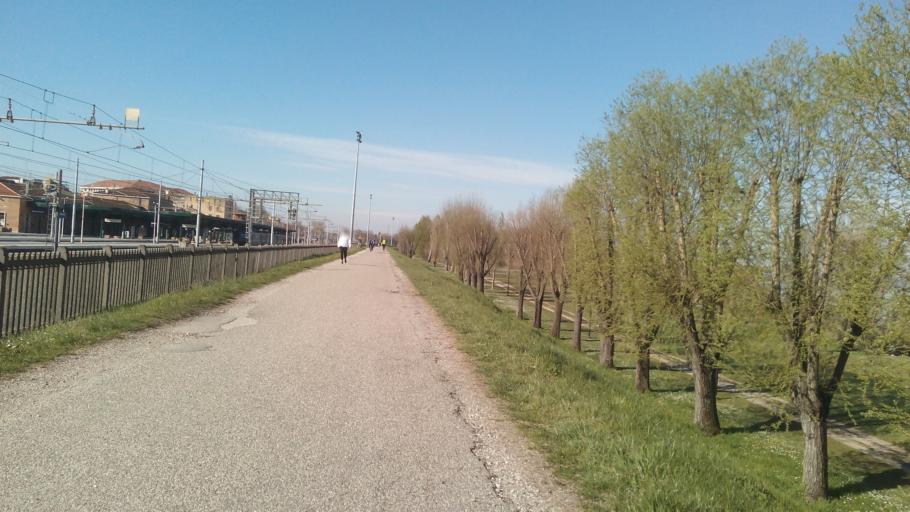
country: IT
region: Lombardy
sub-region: Provincia di Mantova
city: Mantova
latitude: 45.1602
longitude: 10.7853
